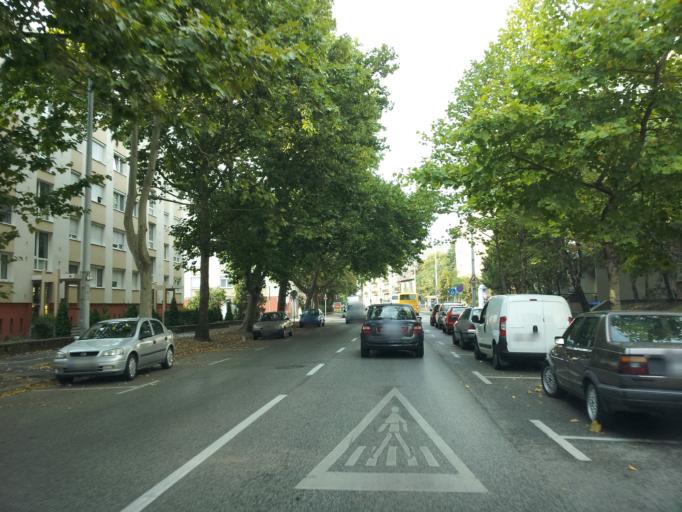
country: HU
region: Gyor-Moson-Sopron
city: Gyor
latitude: 47.6764
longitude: 17.6427
